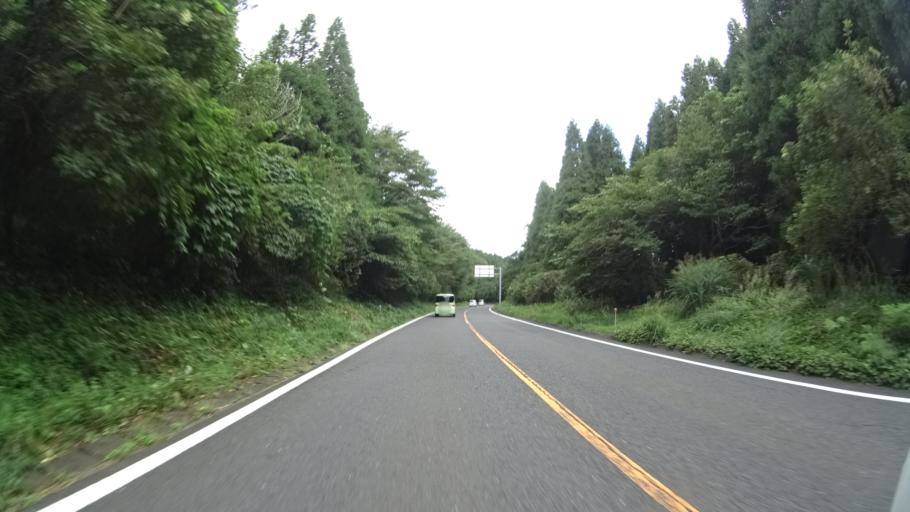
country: JP
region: Oita
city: Tsukawaki
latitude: 33.1897
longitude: 131.2802
